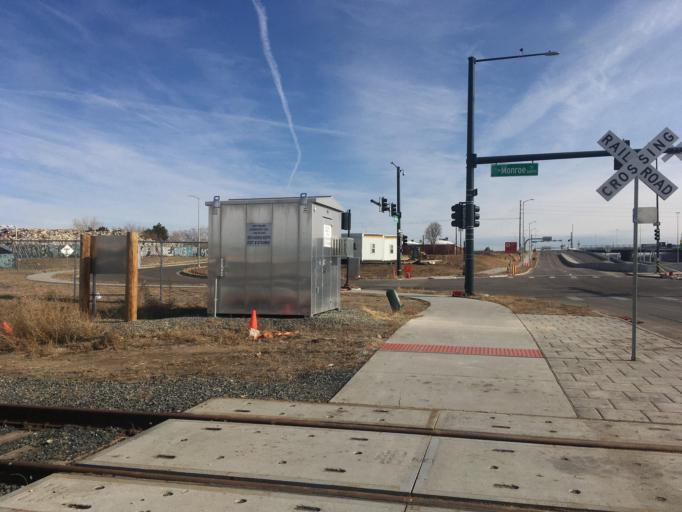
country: US
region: Colorado
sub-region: Adams County
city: Commerce City
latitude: 39.7809
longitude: -104.9457
